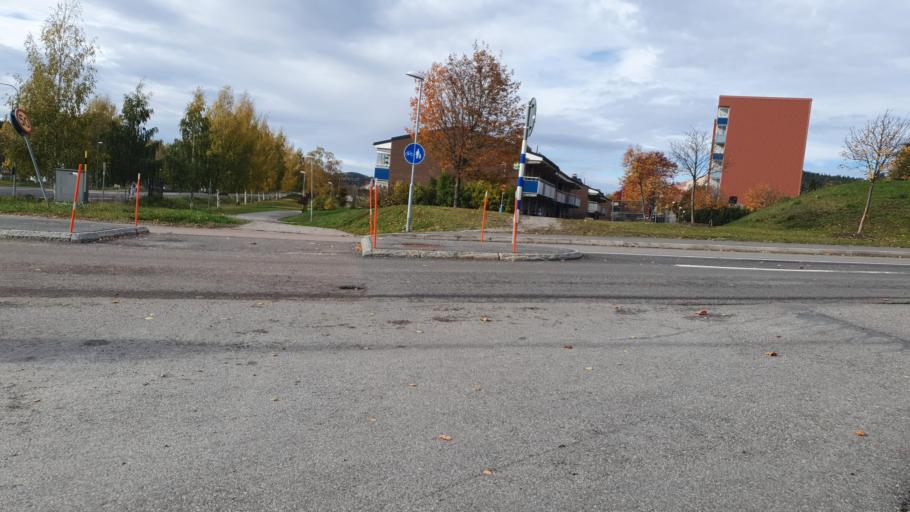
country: SE
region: Vaesternorrland
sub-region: Sundsvalls Kommun
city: Sundsvall
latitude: 62.4123
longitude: 17.2268
